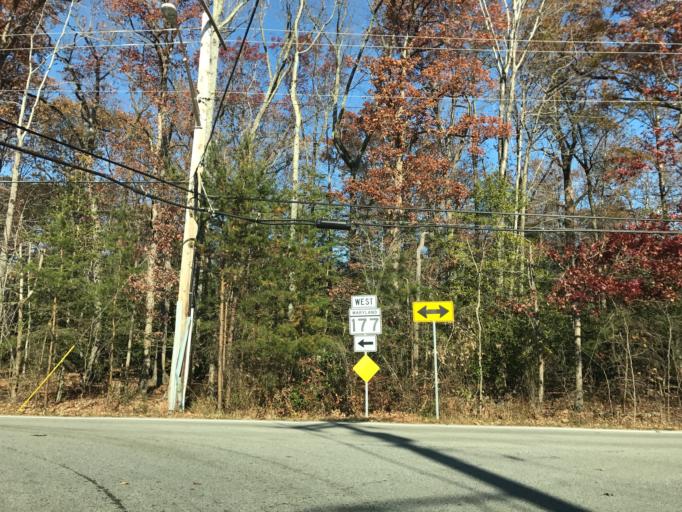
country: US
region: Maryland
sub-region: Anne Arundel County
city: Lake Shore
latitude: 39.1097
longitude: -76.4467
